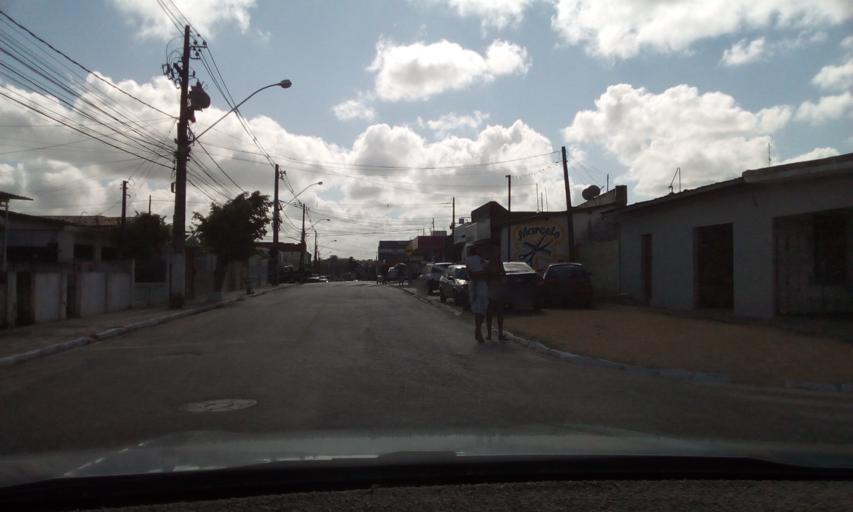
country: BR
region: Paraiba
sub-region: Bayeux
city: Bayeux
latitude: -7.1559
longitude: -34.9020
